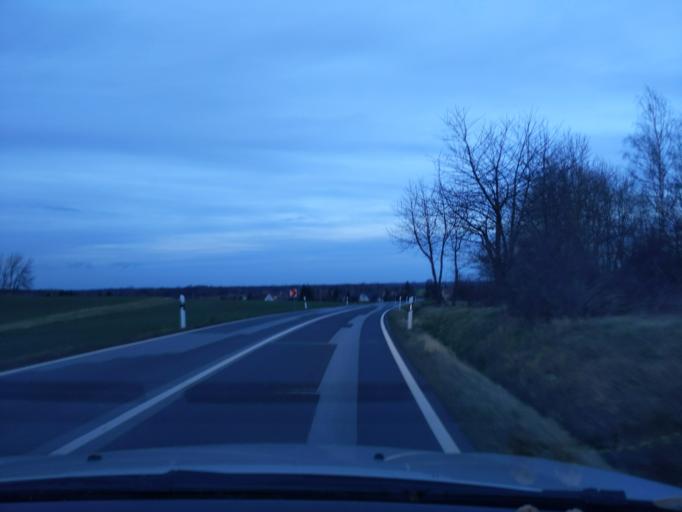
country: DE
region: Saxony
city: Malschwitz
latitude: 51.2168
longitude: 14.4916
